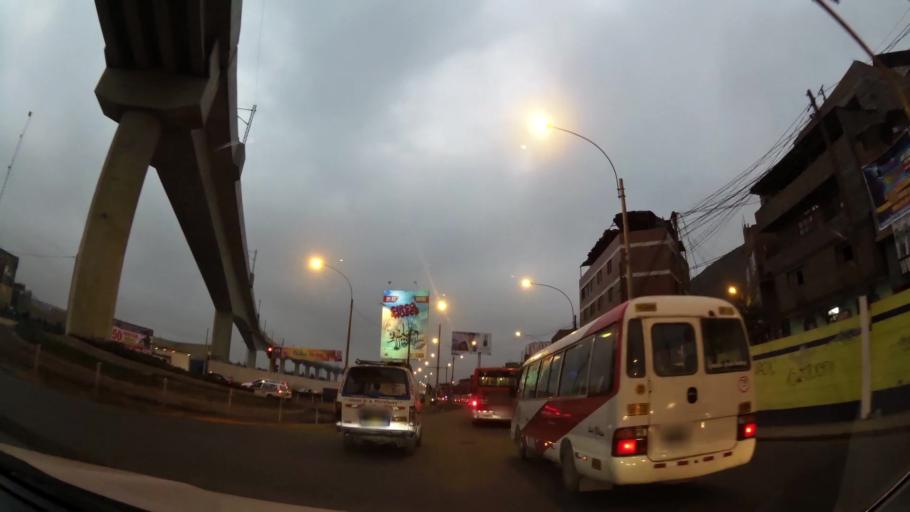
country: PE
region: Lima
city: Lima
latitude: -12.0320
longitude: -77.0122
